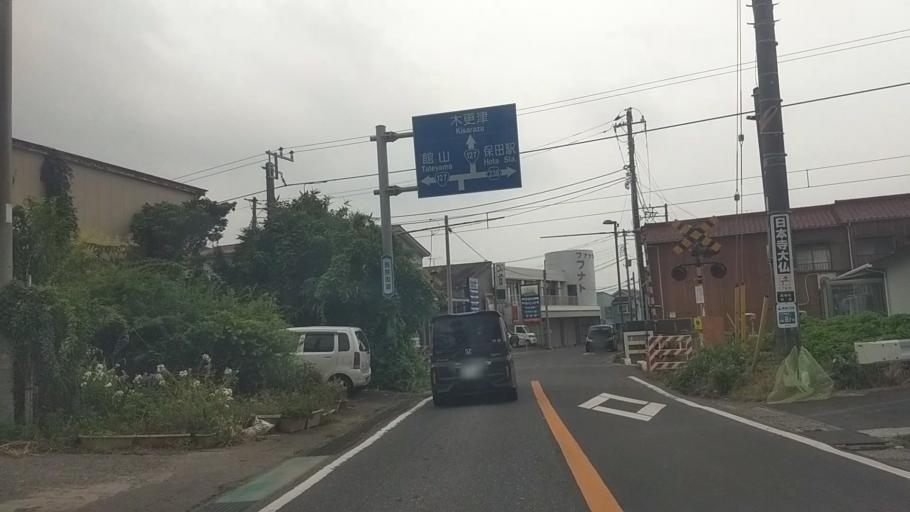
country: JP
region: Chiba
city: Tateyama
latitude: 35.1393
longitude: 139.8404
